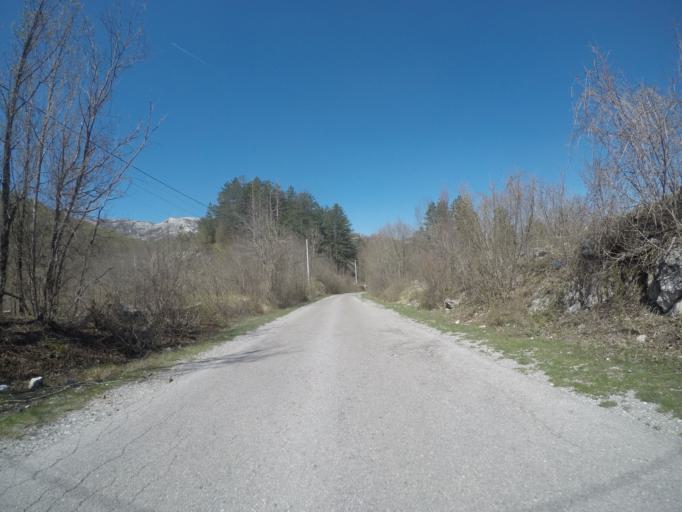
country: ME
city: Dobrota
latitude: 42.4669
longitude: 18.8579
